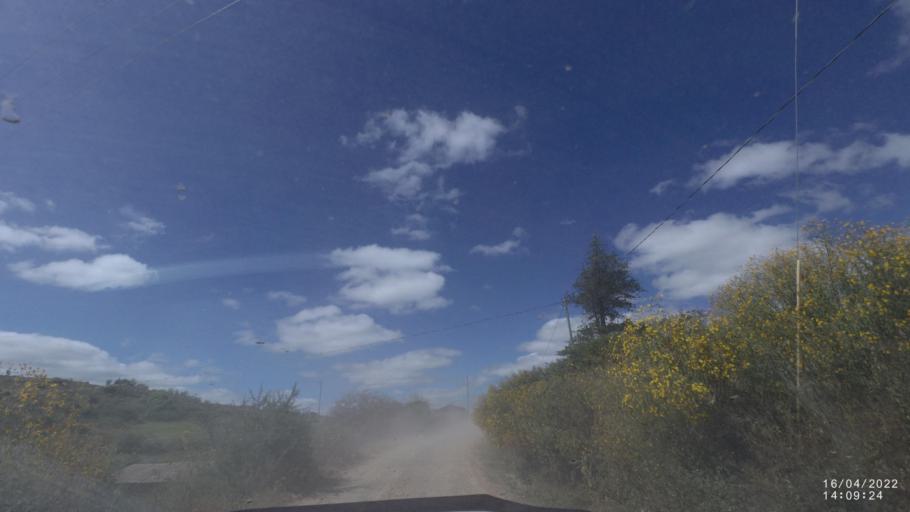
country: BO
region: Cochabamba
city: Mizque
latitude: -18.0605
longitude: -65.5224
